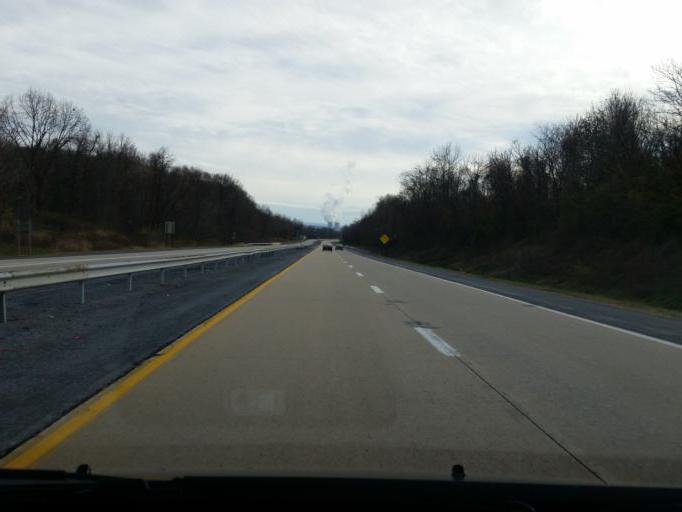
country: US
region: Pennsylvania
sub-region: Dauphin County
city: Middletown
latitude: 40.2216
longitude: -76.7565
